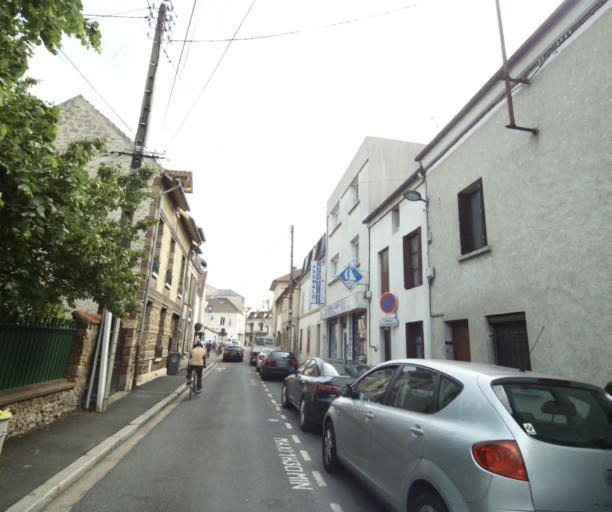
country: FR
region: Ile-de-France
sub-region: Departement des Yvelines
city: Les Mureaux
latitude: 48.9946
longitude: 1.9093
